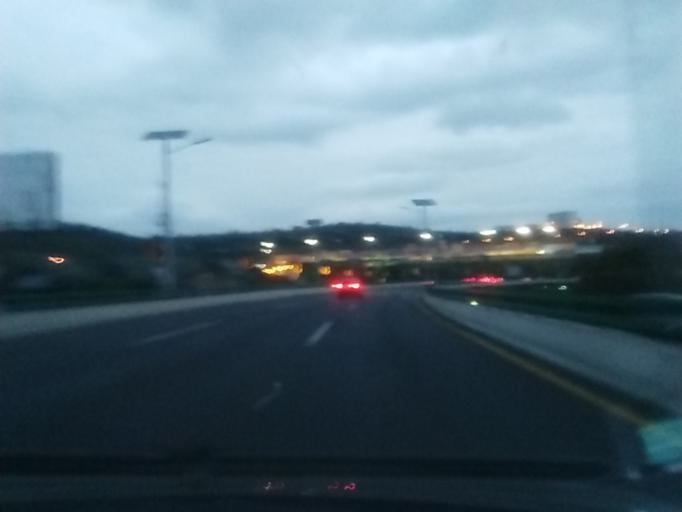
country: MX
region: Mexico
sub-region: Tultitlan
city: Buenavista
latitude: 19.5939
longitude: -99.2018
